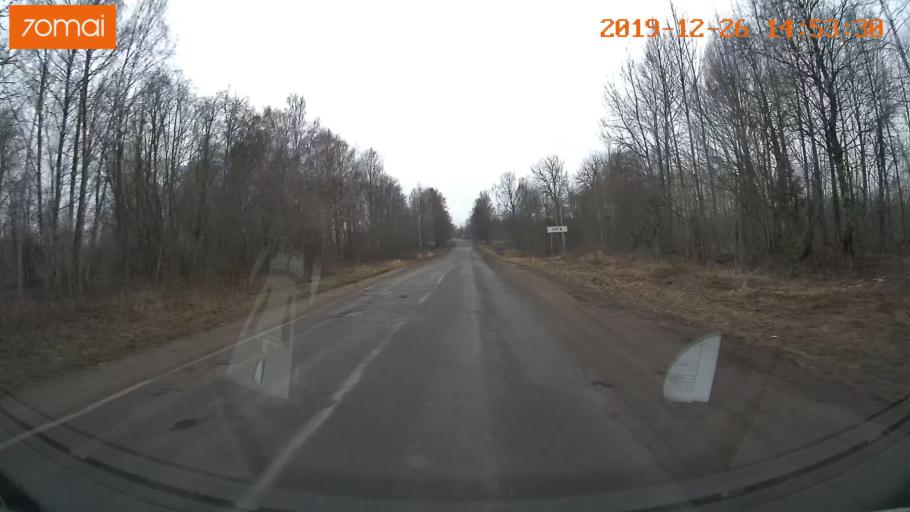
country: RU
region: Jaroslavl
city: Rybinsk
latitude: 58.3145
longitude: 38.8888
